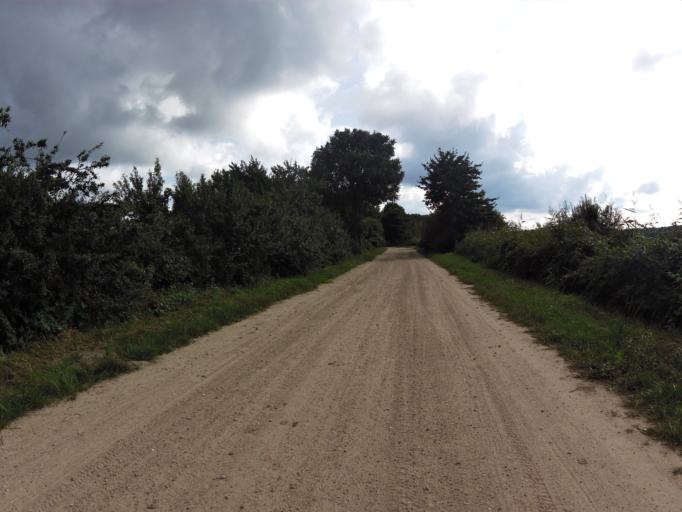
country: DE
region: Mecklenburg-Vorpommern
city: Loddin
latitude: 53.9889
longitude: 14.0573
